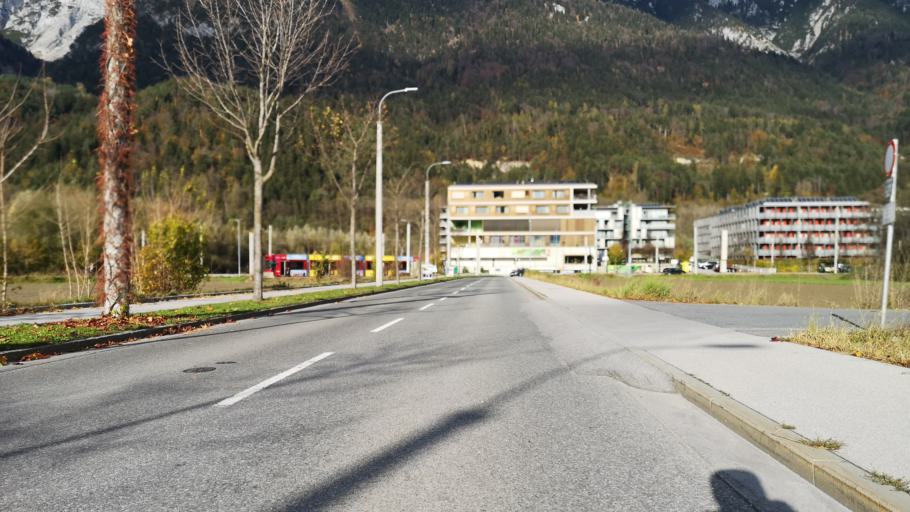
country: AT
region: Tyrol
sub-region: Politischer Bezirk Innsbruck Land
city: Vols
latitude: 47.2637
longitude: 11.3394
